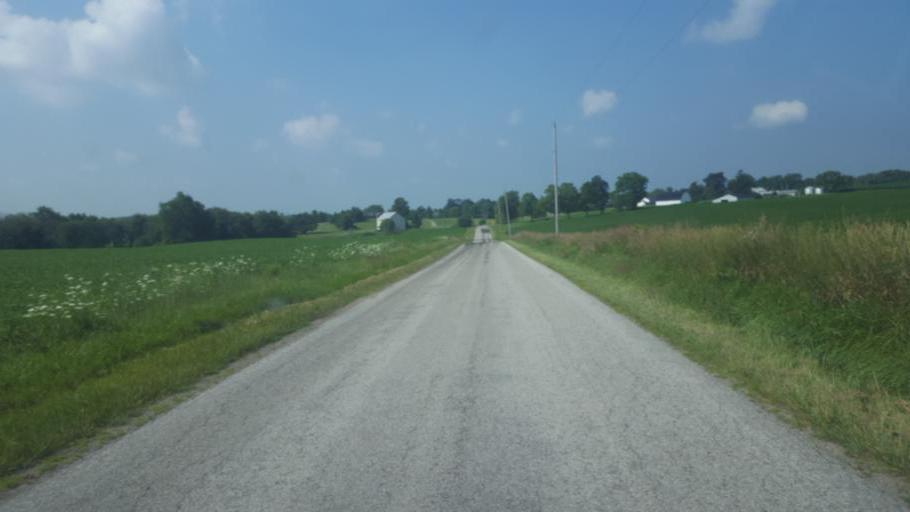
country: US
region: Ohio
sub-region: Richland County
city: Lexington
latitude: 40.6690
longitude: -82.6180
